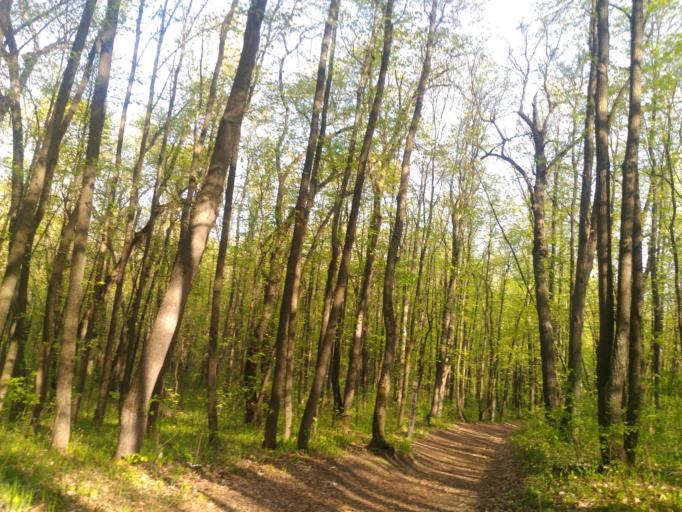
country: RU
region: Ulyanovsk
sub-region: Ulyanovskiy Rayon
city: Ulyanovsk
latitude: 54.2716
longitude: 48.3420
